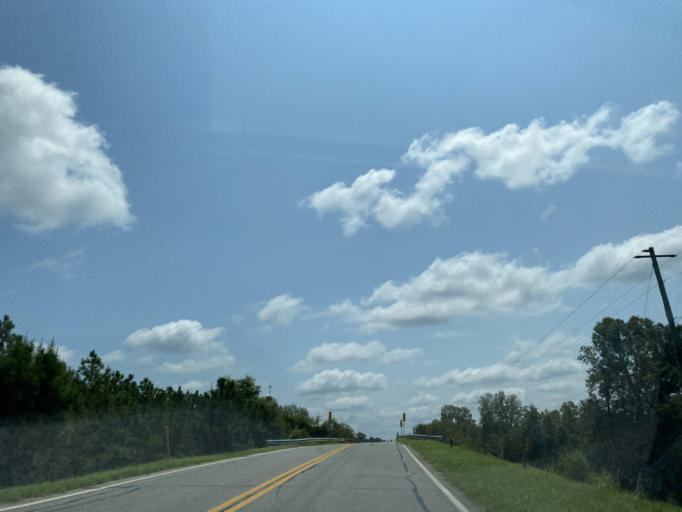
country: US
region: Georgia
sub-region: Wilcox County
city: Abbeville
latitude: 32.0053
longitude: -83.1602
